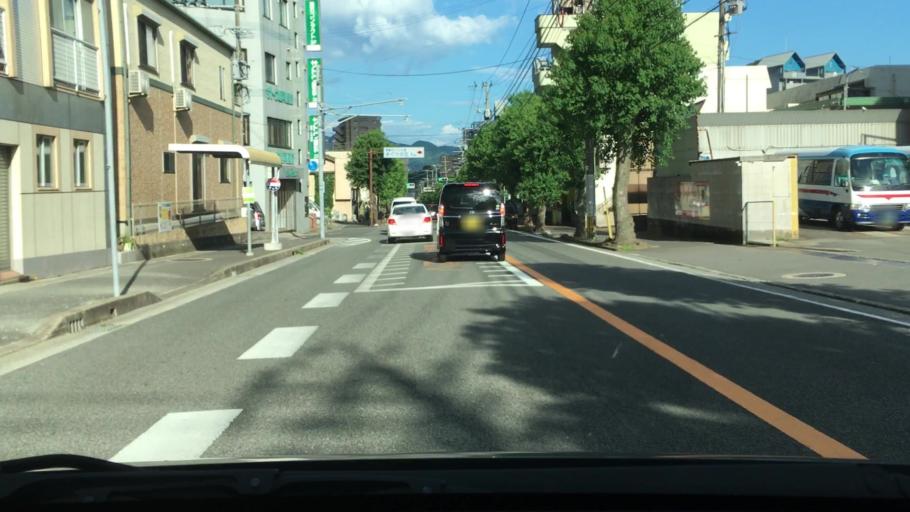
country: JP
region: Nagasaki
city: Togitsu
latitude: 32.8088
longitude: 129.8312
